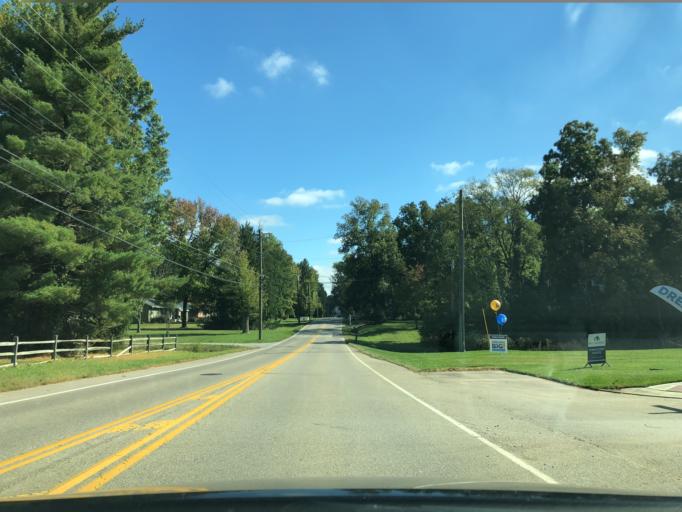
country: US
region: Ohio
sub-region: Hamilton County
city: Loveland
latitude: 39.2357
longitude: -84.2638
